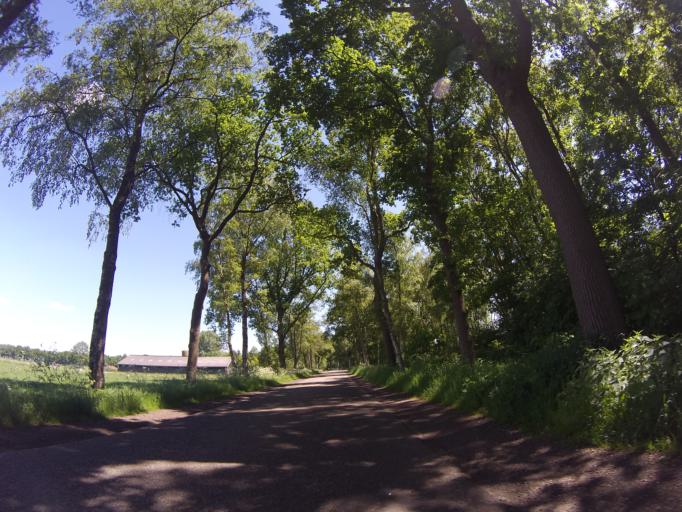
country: NL
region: Drenthe
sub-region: Gemeente Hoogeveen
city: Hoogeveen
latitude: 52.7893
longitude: 6.5721
